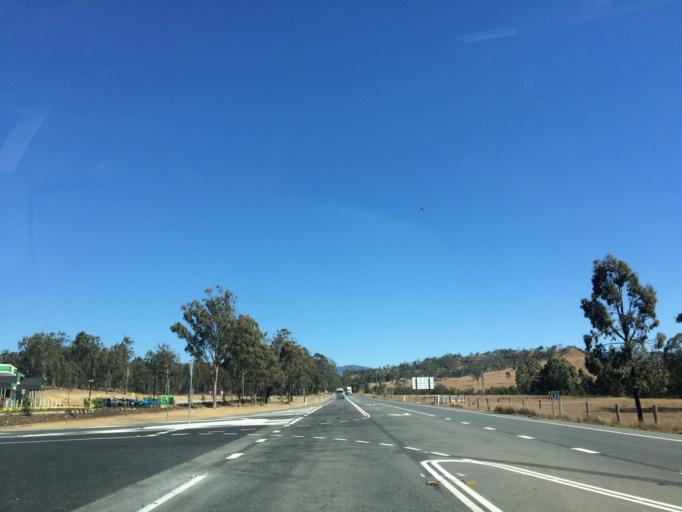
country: AU
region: Queensland
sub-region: Ipswich
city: Thagoona
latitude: -27.9908
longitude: 152.5392
